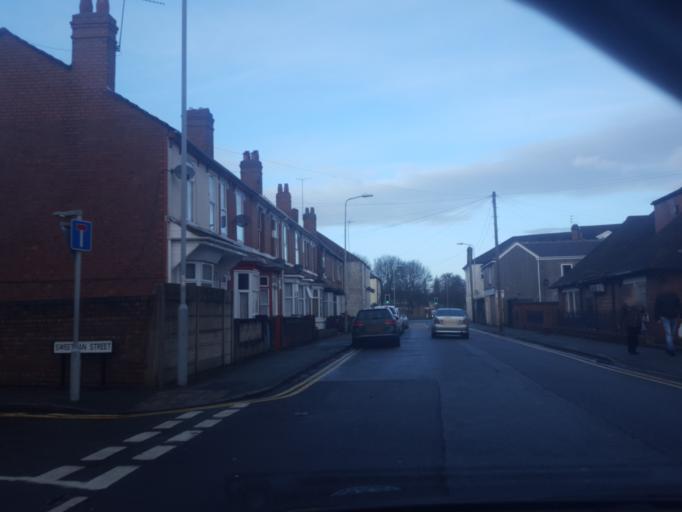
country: GB
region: England
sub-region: Wolverhampton
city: Wolverhampton
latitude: 52.5929
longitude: -2.1456
